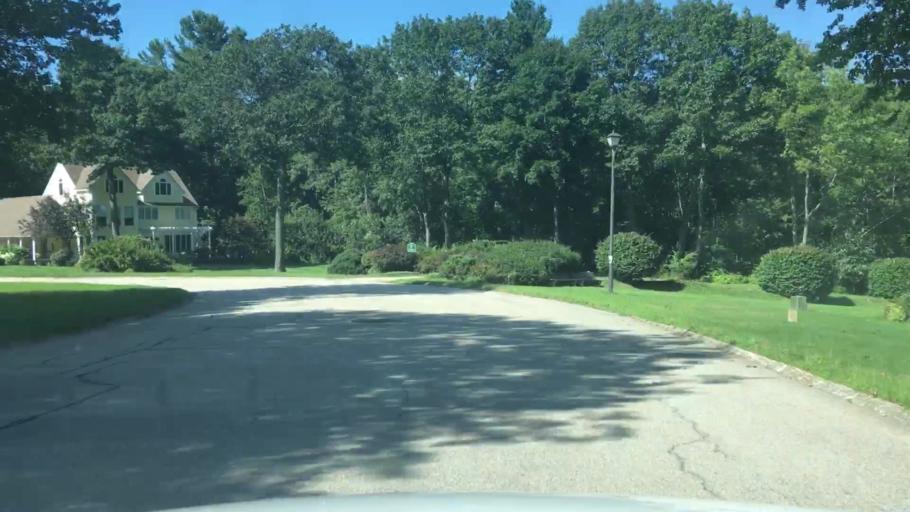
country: US
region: Maine
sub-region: York County
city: Eliot
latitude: 43.1705
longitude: -70.8319
